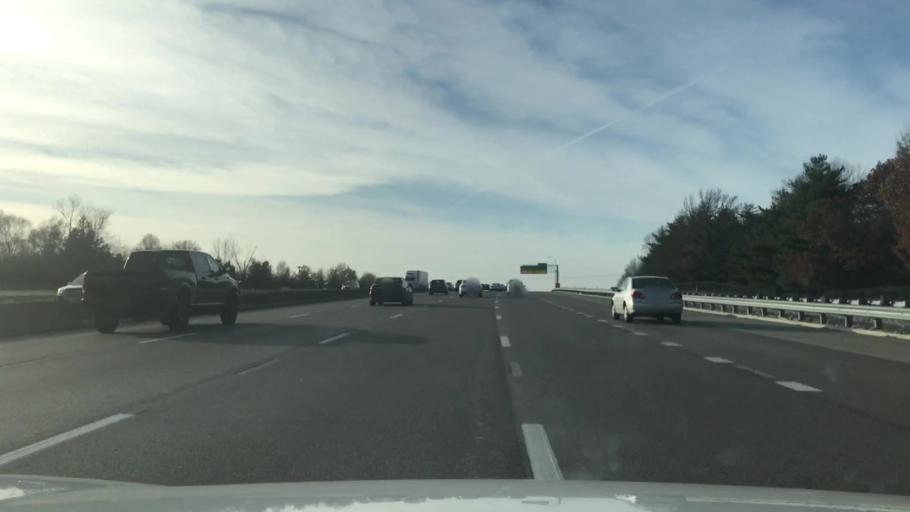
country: US
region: Missouri
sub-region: Saint Louis County
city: Town and Country
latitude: 38.6388
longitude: -90.4917
